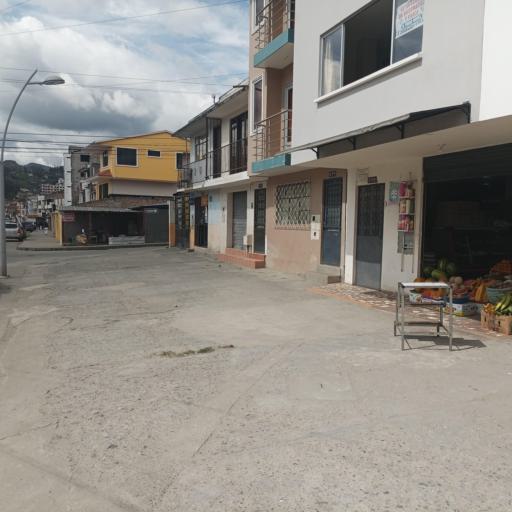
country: EC
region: Loja
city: Loja
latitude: -3.9809
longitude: -79.2013
